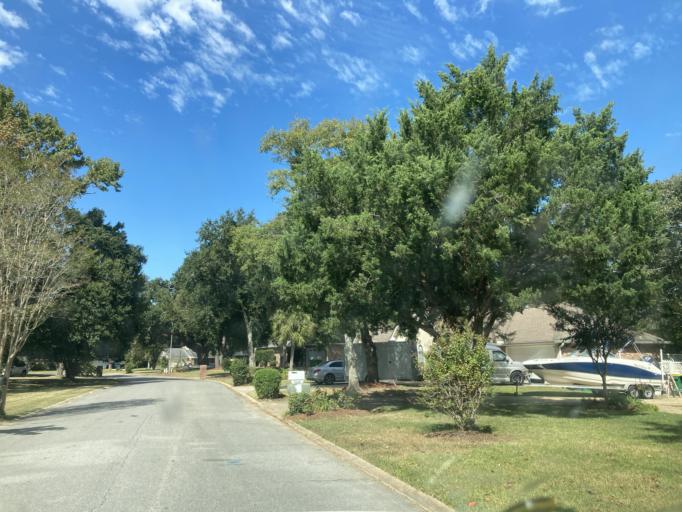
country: US
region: Mississippi
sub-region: Jackson County
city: Gulf Hills
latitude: 30.4390
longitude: -88.8527
